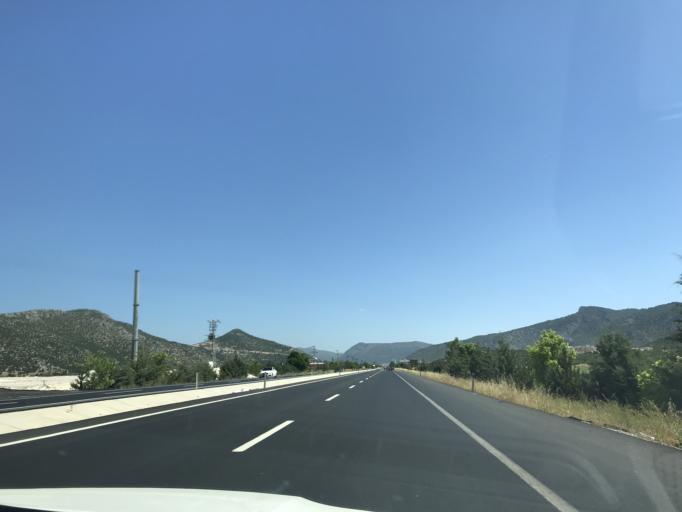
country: TR
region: Burdur
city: Bucak
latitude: 37.3923
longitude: 30.5337
